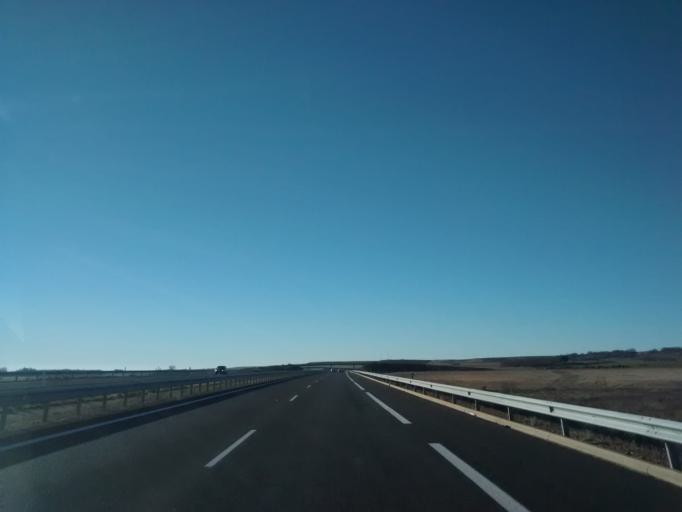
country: ES
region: Castille and Leon
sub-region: Provincia de Palencia
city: Espinosa de Villagonzalo
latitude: 42.4971
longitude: -4.3815
